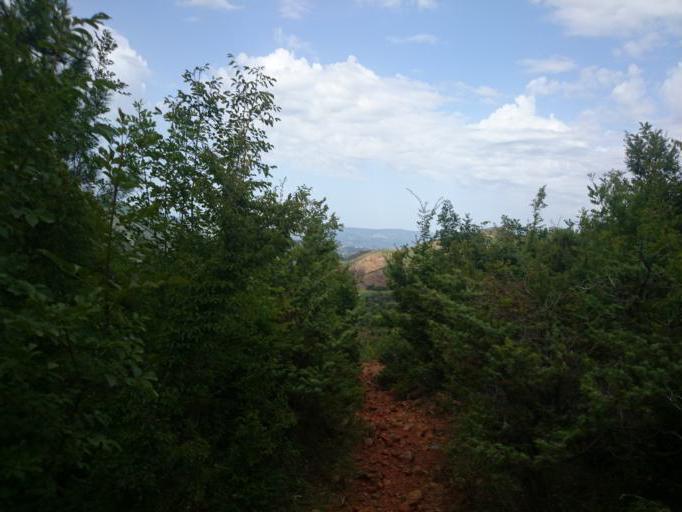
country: AL
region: Elbasan
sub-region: Rrethi i Gramshit
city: Lenias
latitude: 40.7741
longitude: 20.3270
